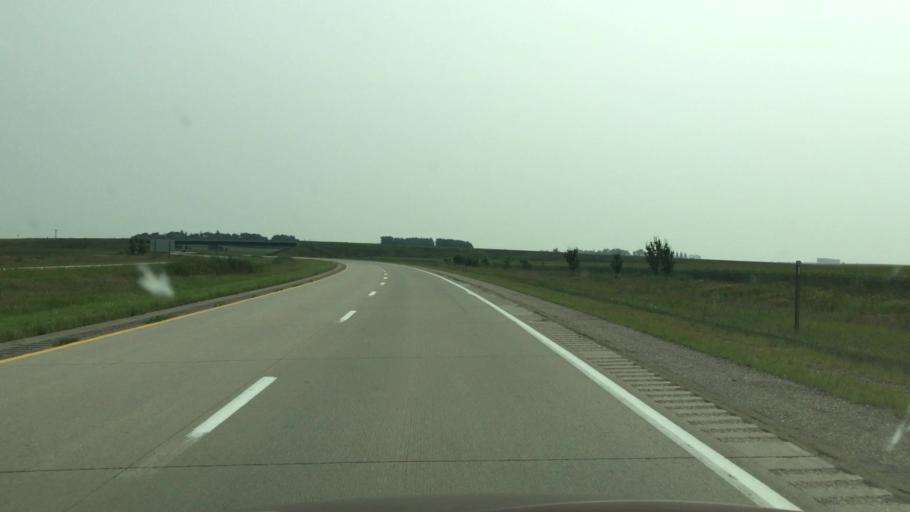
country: US
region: Iowa
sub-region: Osceola County
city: Sibley
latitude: 43.3850
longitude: -95.7278
